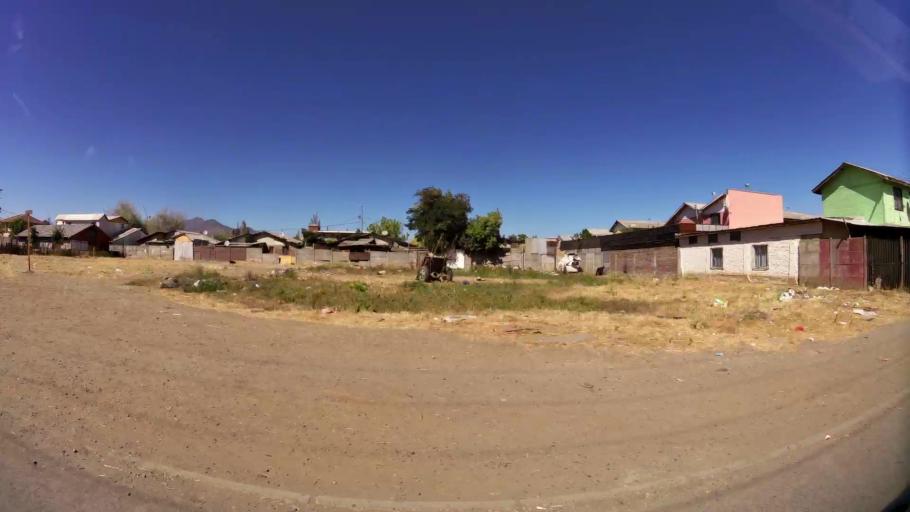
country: CL
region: O'Higgins
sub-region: Provincia de Cachapoal
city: Rancagua
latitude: -34.1669
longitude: -70.7016
